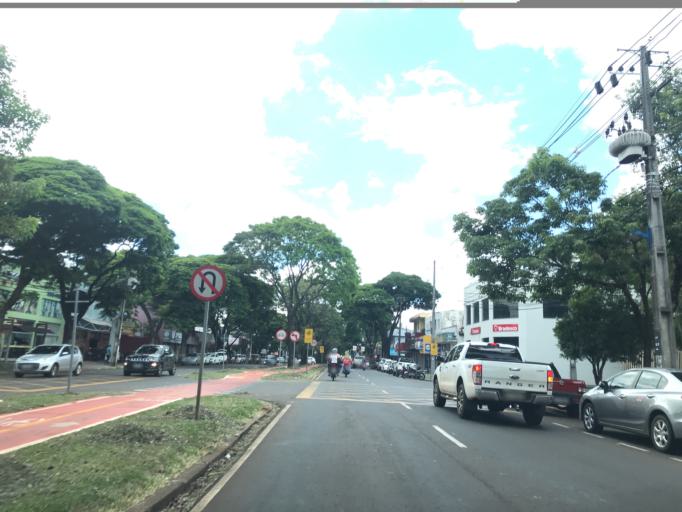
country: BR
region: Parana
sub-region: Maringa
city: Maringa
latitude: -23.4110
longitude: -51.9244
